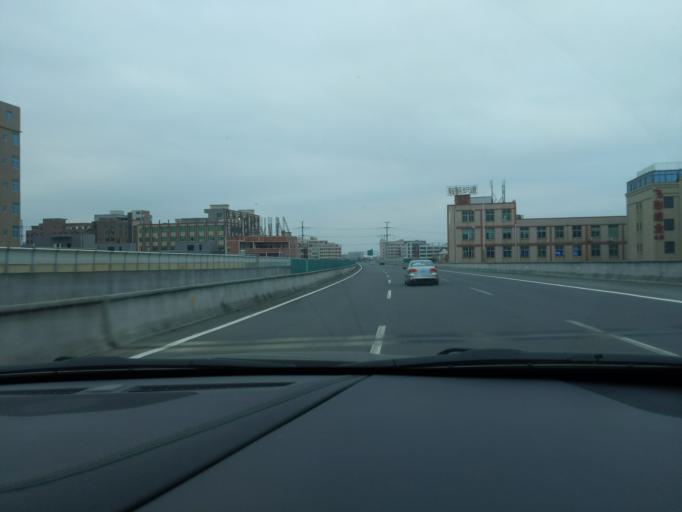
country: CN
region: Fujian
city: Shishi
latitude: 24.7573
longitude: 118.6098
